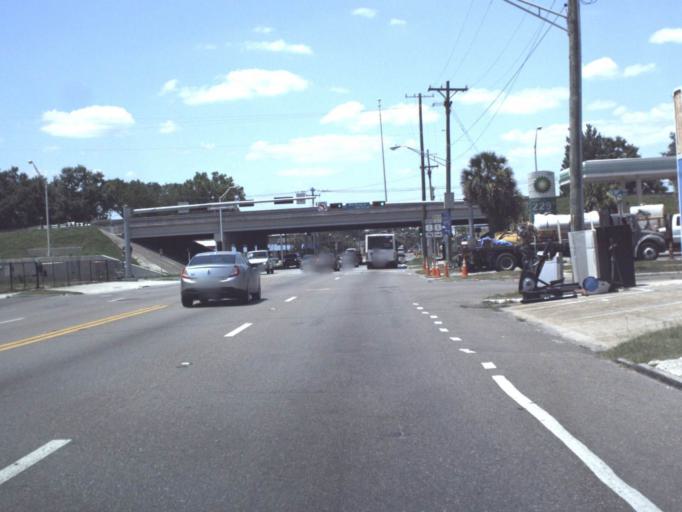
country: US
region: Florida
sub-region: Duval County
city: Jacksonville
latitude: 30.3553
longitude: -81.6538
